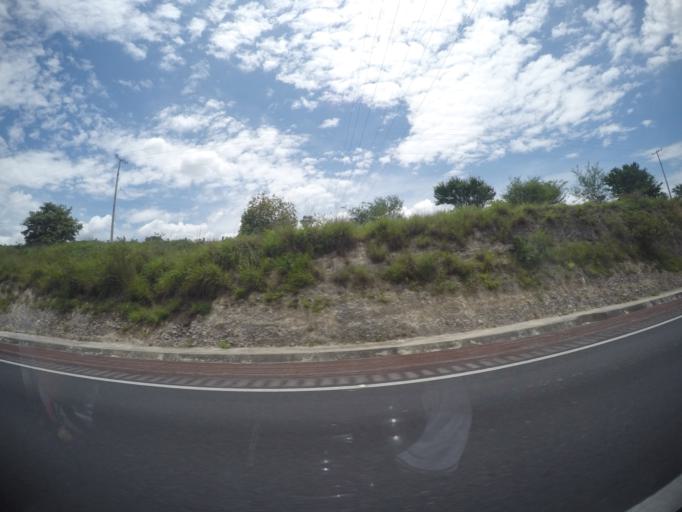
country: MX
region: Guerrero
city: Petaquillas
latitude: 17.5011
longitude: -99.4794
